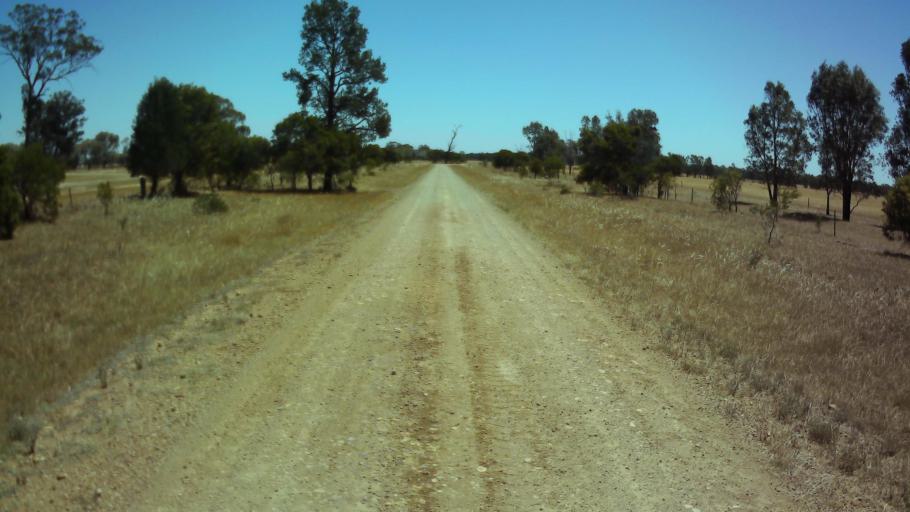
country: AU
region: New South Wales
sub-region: Weddin
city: Grenfell
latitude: -33.9873
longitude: 147.9299
